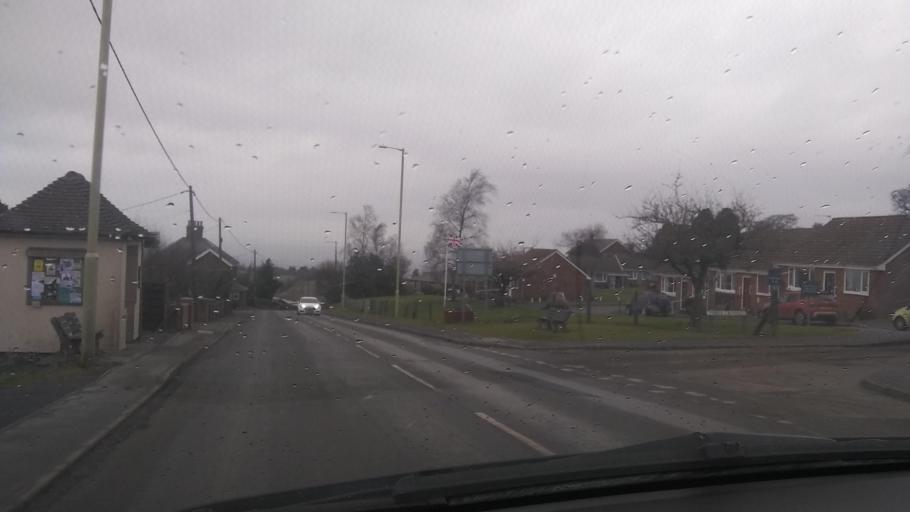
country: GB
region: England
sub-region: Worcestershire
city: Tenbury Wells
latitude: 52.3746
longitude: -2.6012
